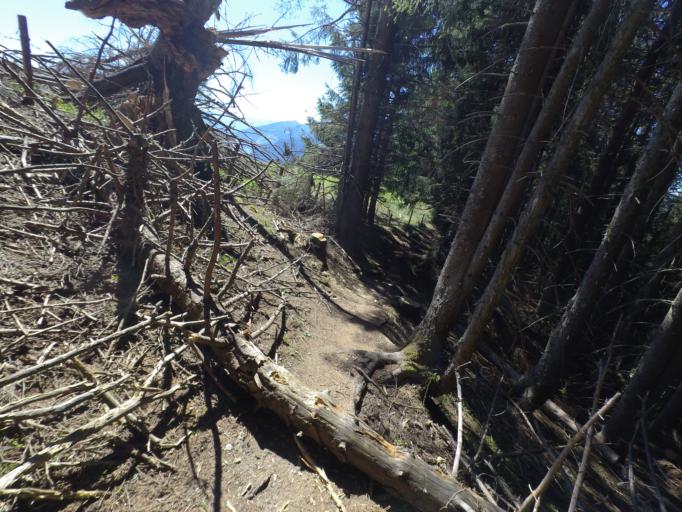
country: AT
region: Salzburg
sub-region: Politischer Bezirk Sankt Johann im Pongau
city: Goldegg
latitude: 47.3426
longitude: 13.0644
